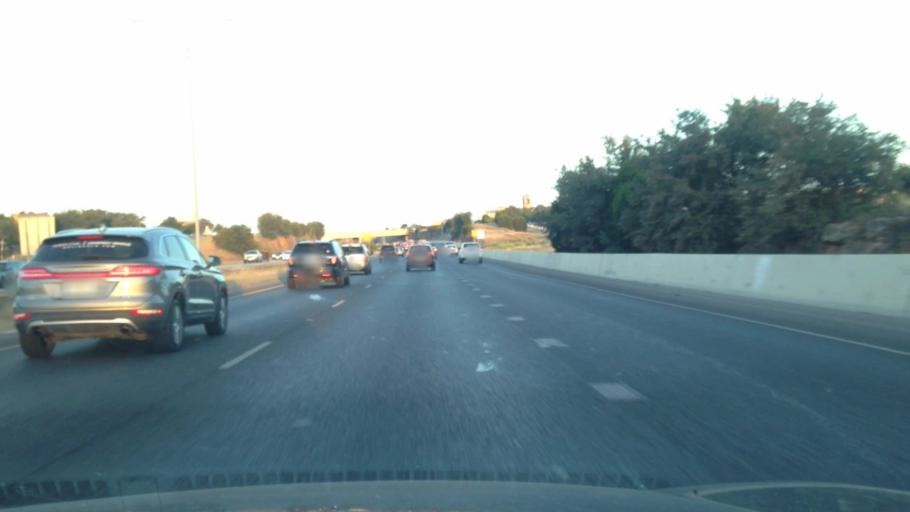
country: US
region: Texas
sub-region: Bexar County
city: Hollywood Park
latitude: 29.6092
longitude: -98.5181
